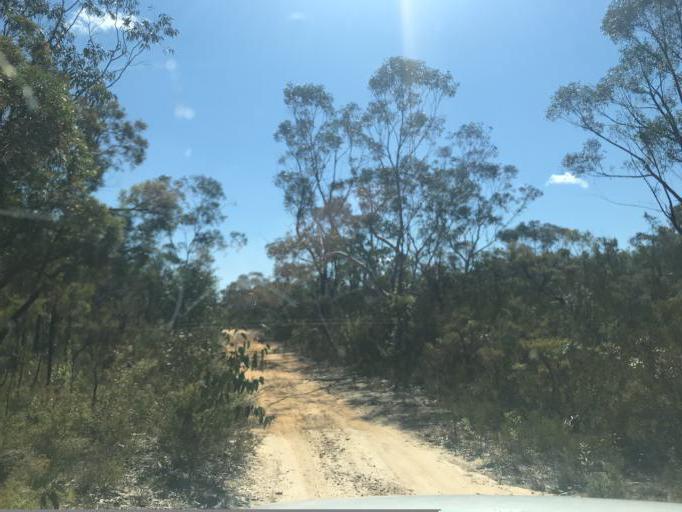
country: AU
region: New South Wales
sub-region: Wyong Shire
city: Little Jilliby
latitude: -33.1598
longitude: 151.0989
